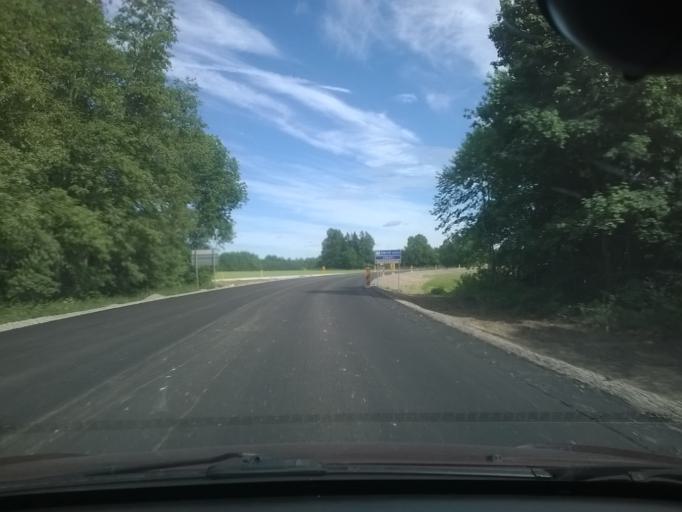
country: EE
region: Harju
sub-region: Anija vald
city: Kehra
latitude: 59.2832
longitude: 25.2621
